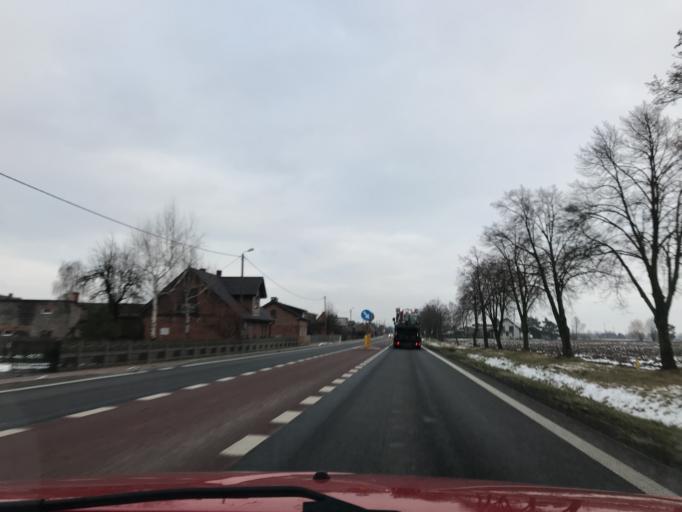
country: PL
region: Greater Poland Voivodeship
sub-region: Powiat pleszewski
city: Goluchow
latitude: 51.8692
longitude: 17.8965
